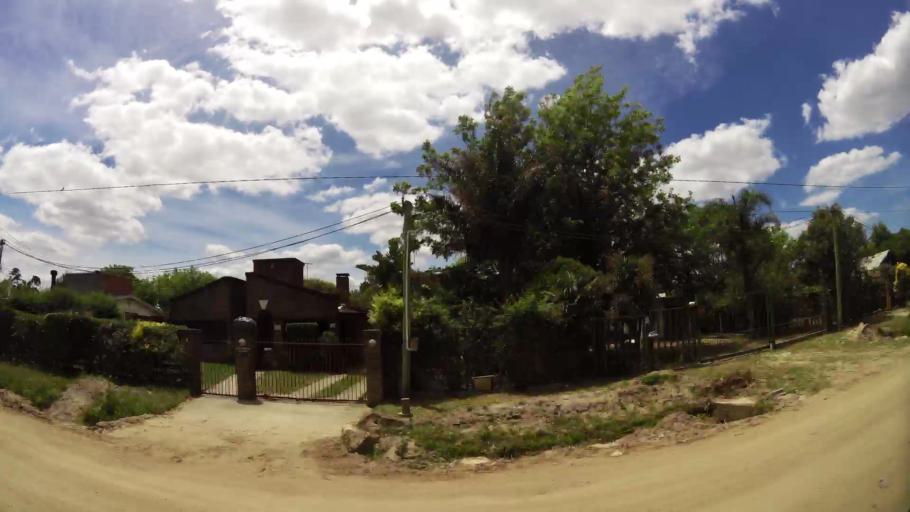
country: UY
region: Canelones
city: Colonia Nicolich
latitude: -34.8293
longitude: -55.9828
